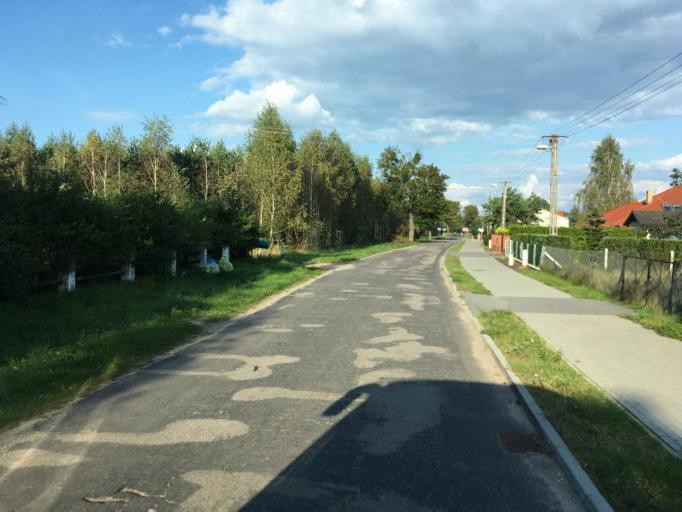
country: PL
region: Kujawsko-Pomorskie
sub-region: Powiat tucholski
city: Gostycyn
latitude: 53.5095
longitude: 17.8767
